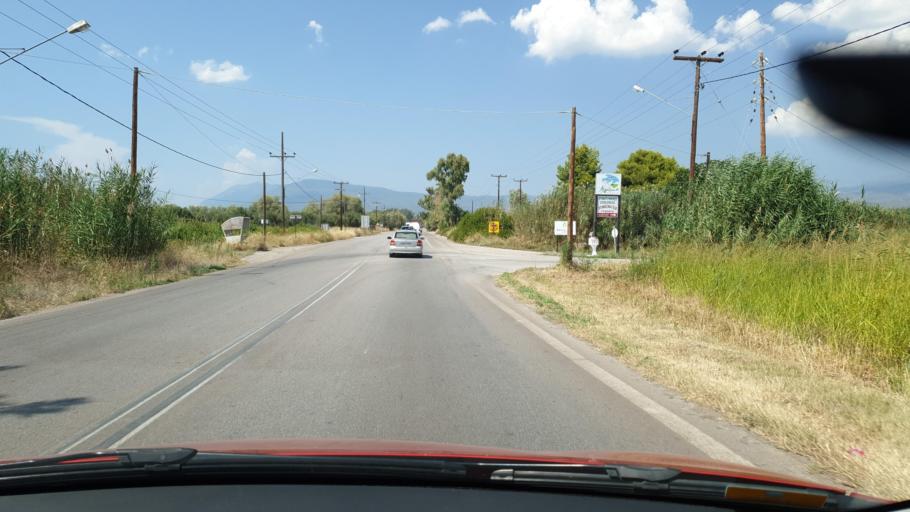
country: GR
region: Central Greece
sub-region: Nomos Evvoias
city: Nea Artaki
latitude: 38.5373
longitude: 23.6310
